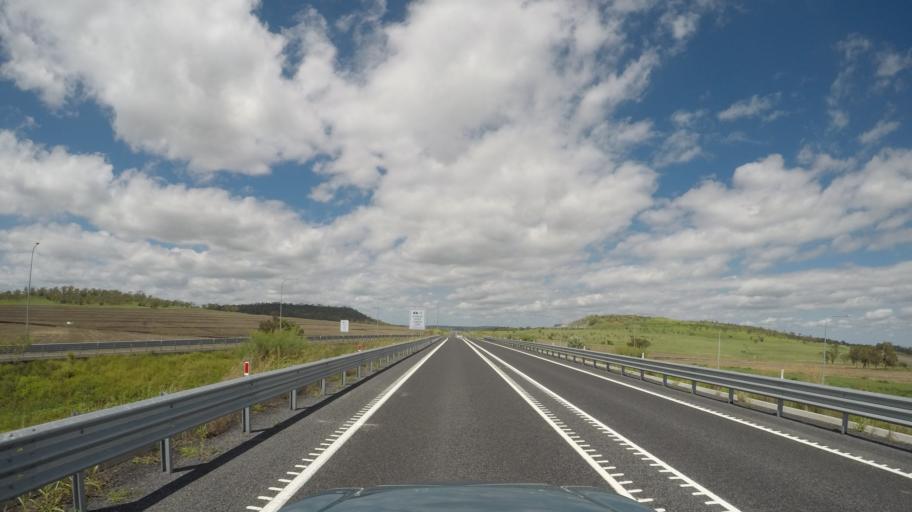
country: AU
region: Queensland
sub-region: Toowoomba
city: Westbrook
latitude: -27.5481
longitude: 151.8327
